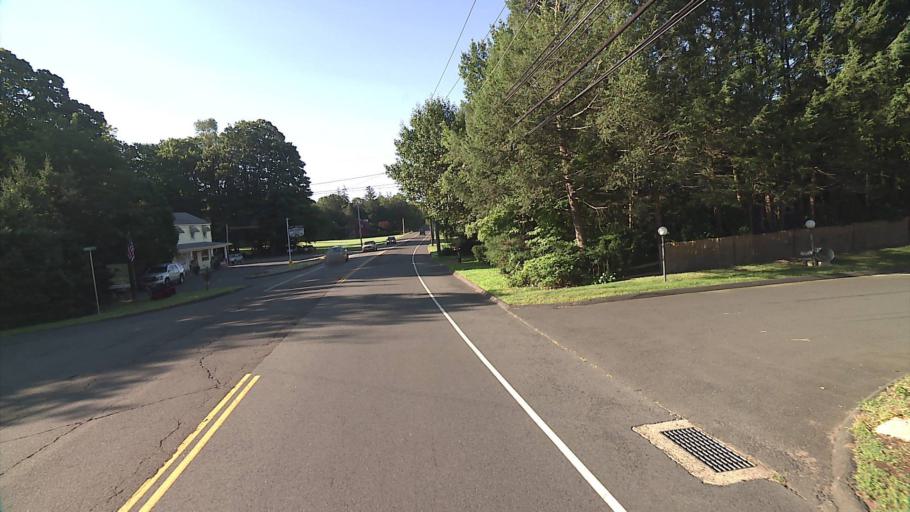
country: US
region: Connecticut
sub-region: New Haven County
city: Hamden
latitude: 41.4287
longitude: -72.9064
